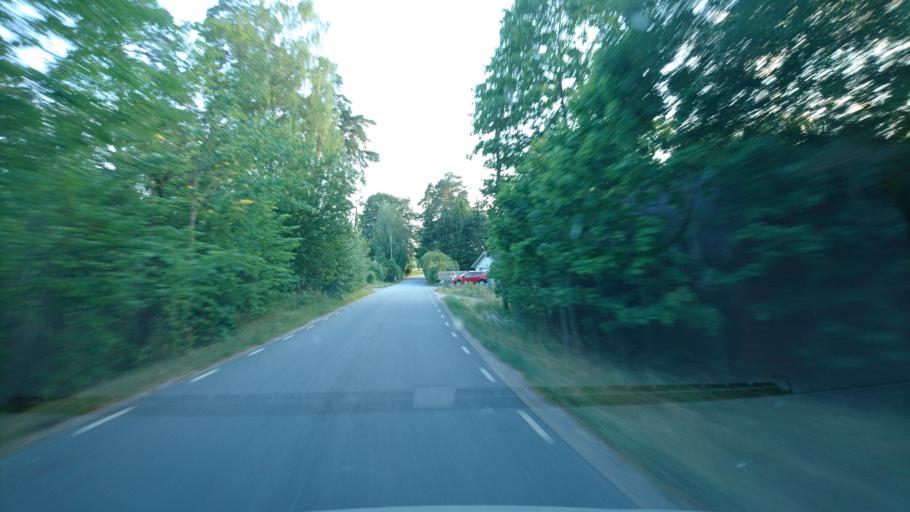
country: SE
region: Uppsala
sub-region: Uppsala Kommun
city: Saevja
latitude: 59.8093
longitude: 17.6774
